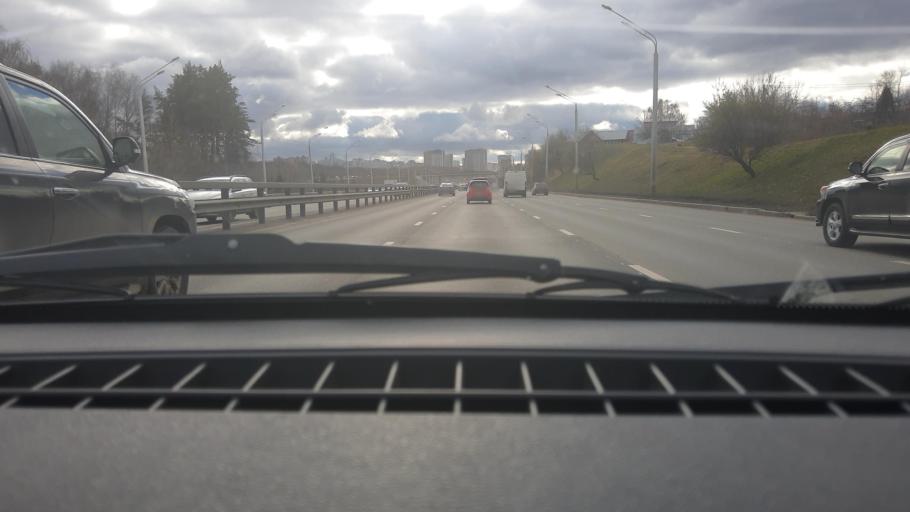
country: RU
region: Bashkortostan
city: Ufa
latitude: 54.7442
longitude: 56.0084
